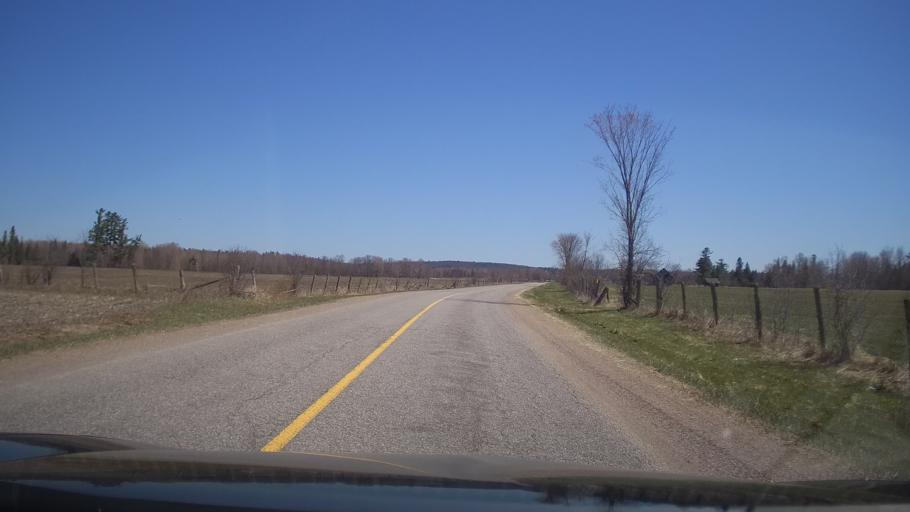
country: CA
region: Quebec
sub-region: Outaouais
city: Shawville
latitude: 45.5440
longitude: -76.3900
